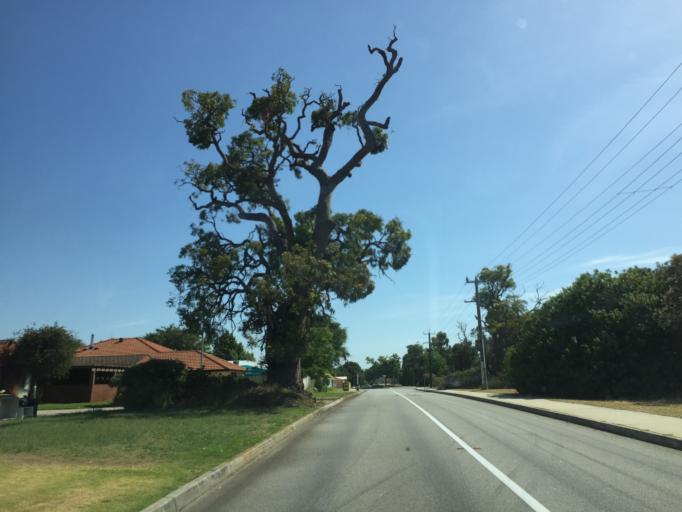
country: AU
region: Western Australia
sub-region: Gosnells
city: Thornlie
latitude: -32.0824
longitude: 115.9600
